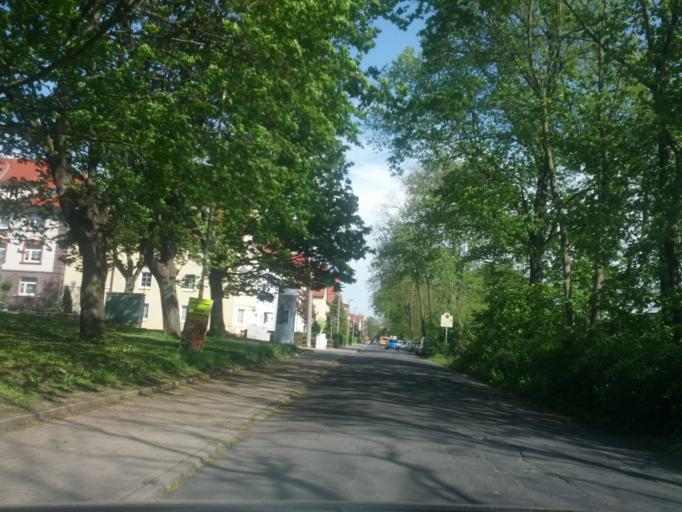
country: DE
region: Thuringia
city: Eisenach
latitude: 50.9826
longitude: 10.3211
